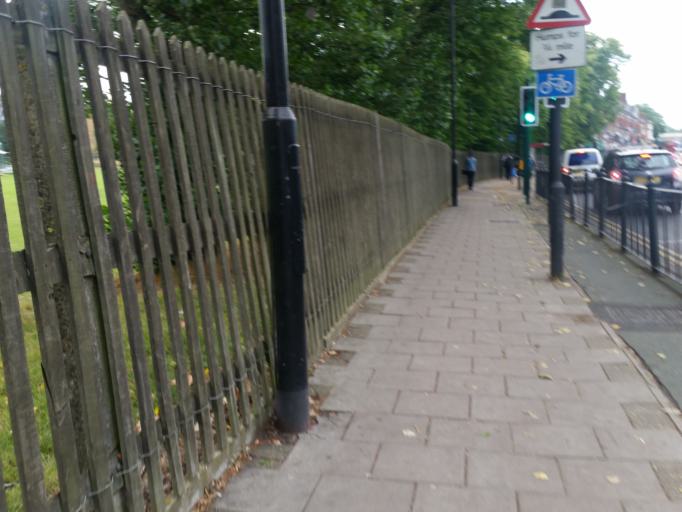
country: GB
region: England
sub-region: Greater London
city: Harringay
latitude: 51.5745
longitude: -0.0982
